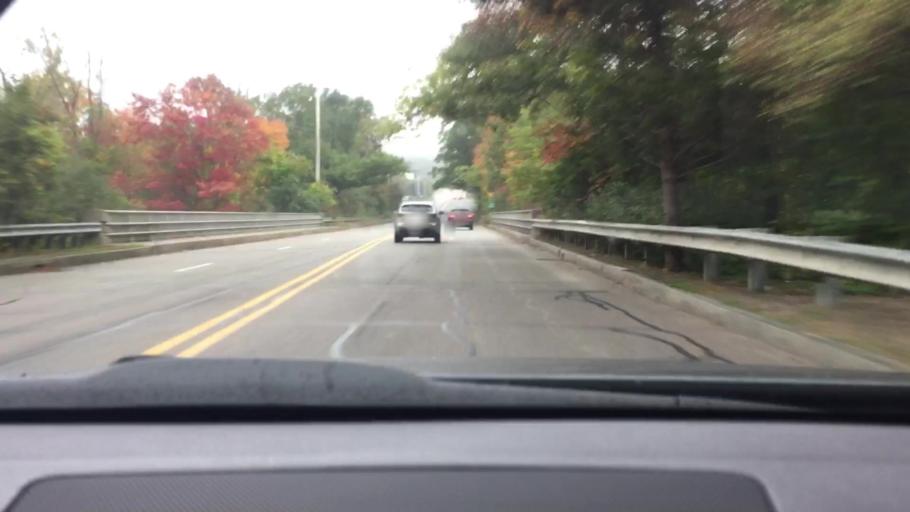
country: US
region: Massachusetts
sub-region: Norfolk County
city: Needham
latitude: 42.2974
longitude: -71.2074
